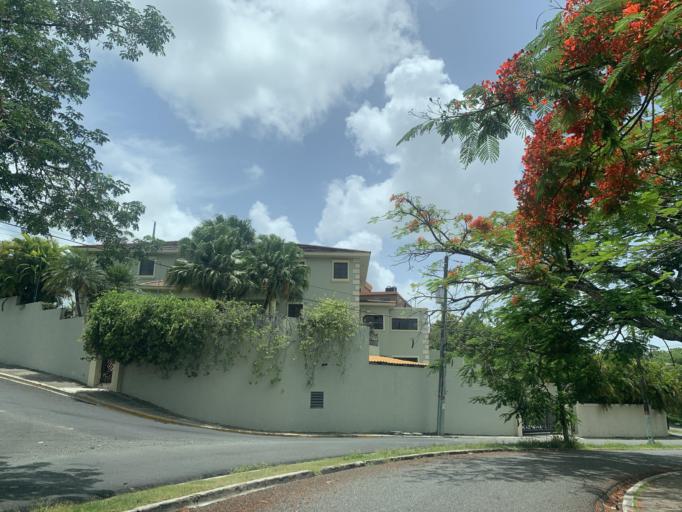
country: DO
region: Nacional
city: La Agustina
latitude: 18.5004
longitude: -69.9524
